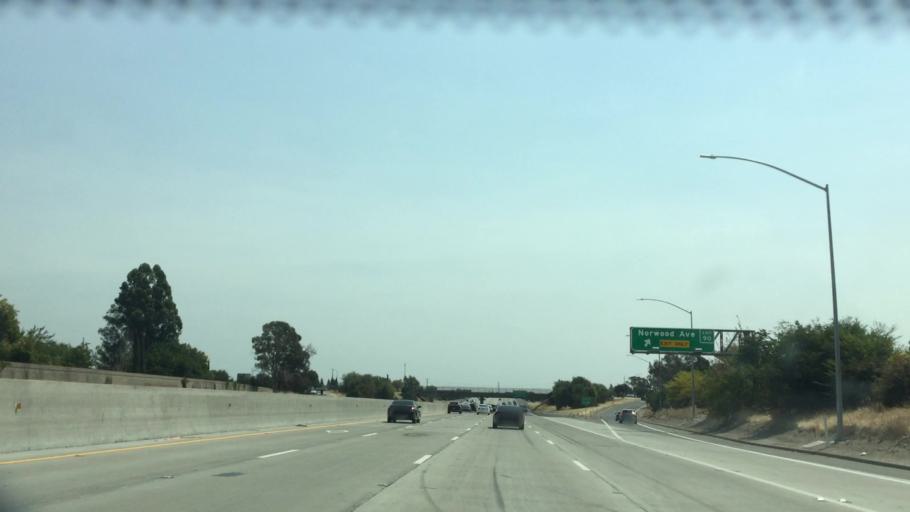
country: US
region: California
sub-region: Sacramento County
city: Rio Linda
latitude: 38.6415
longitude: -121.4617
